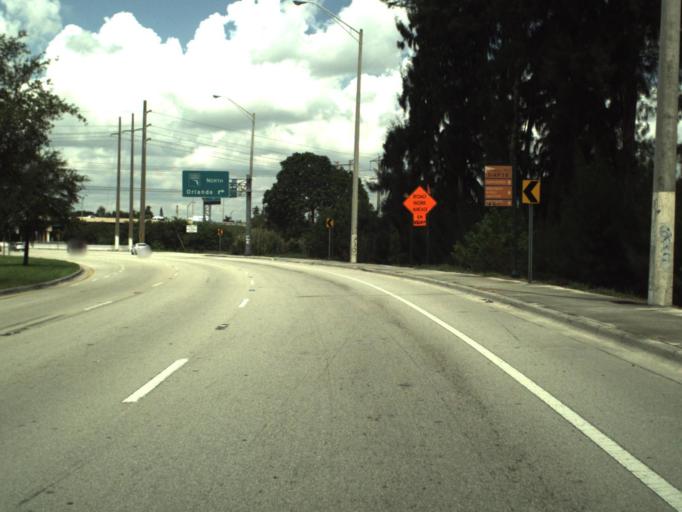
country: US
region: Florida
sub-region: Broward County
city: Davie
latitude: 26.0649
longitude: -80.2130
